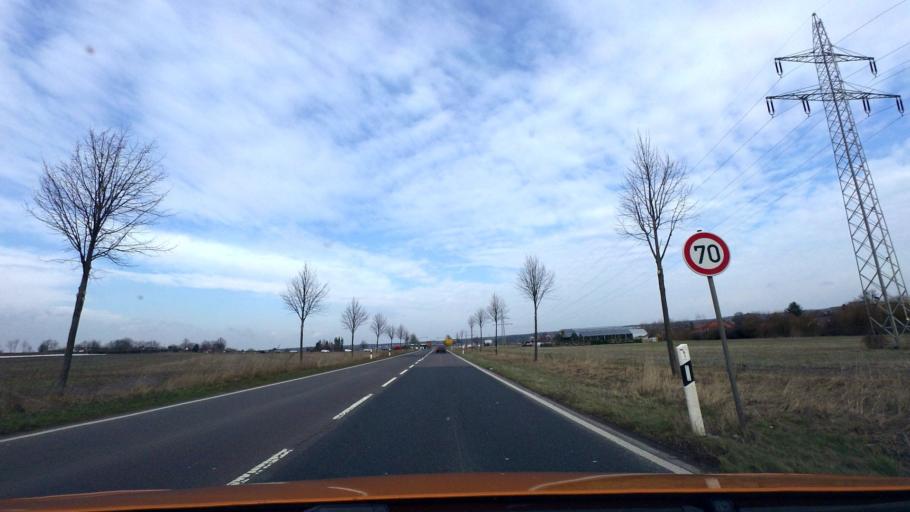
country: DE
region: Lower Saxony
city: Helmstedt
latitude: 52.2265
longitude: 10.9914
